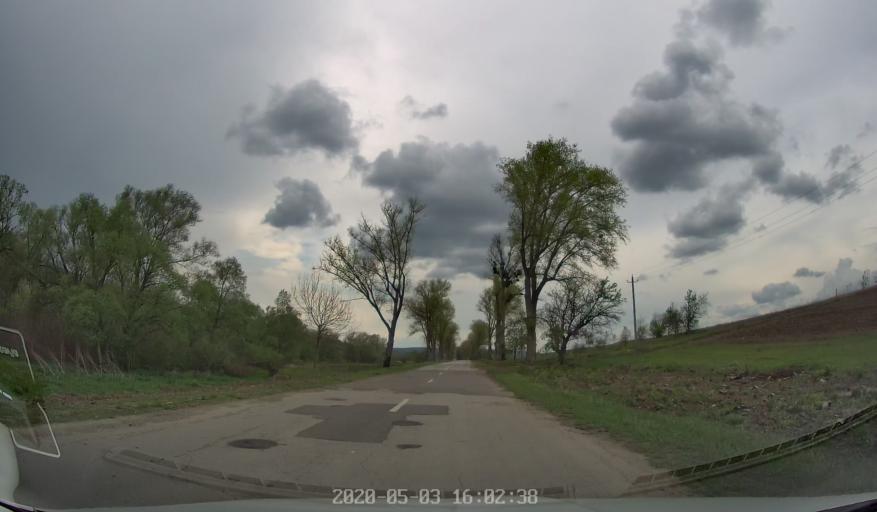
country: MD
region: Stinga Nistrului
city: Bucovat
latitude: 47.1743
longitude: 28.3928
